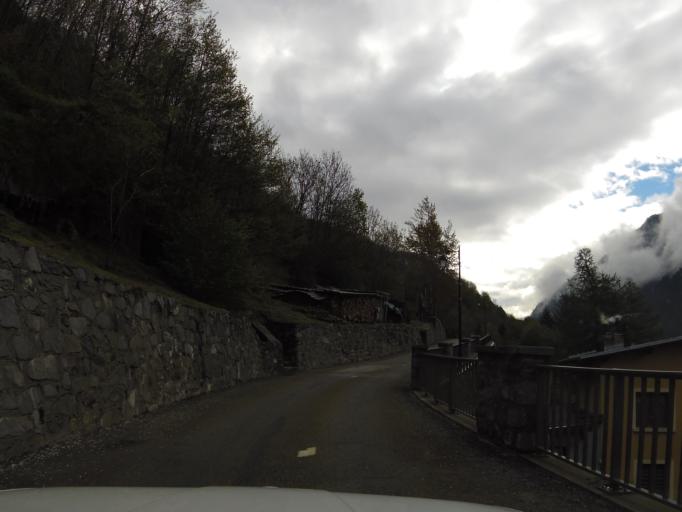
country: FR
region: Rhone-Alpes
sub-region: Departement de la Savoie
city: Saint-Michel-de-Maurienne
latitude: 45.2100
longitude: 6.5358
